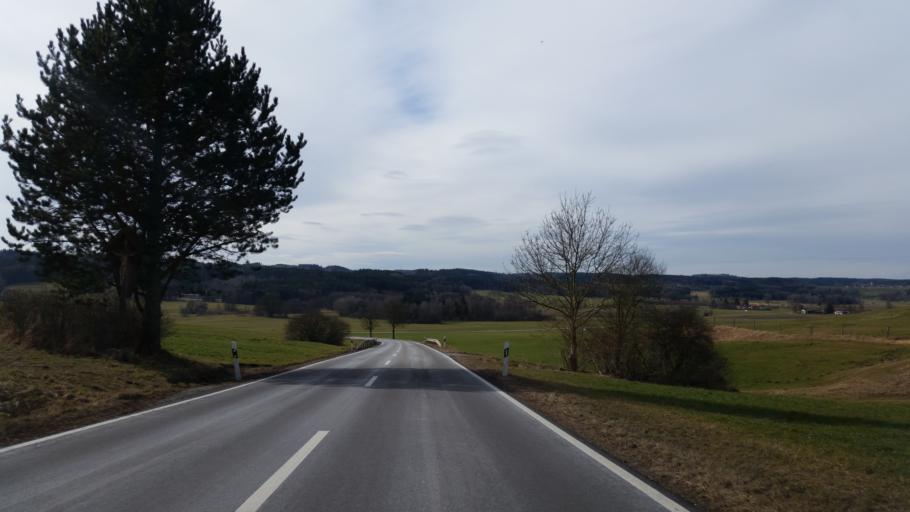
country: DE
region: Bavaria
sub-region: Upper Bavaria
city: Glonn
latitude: 47.9467
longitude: 11.9114
